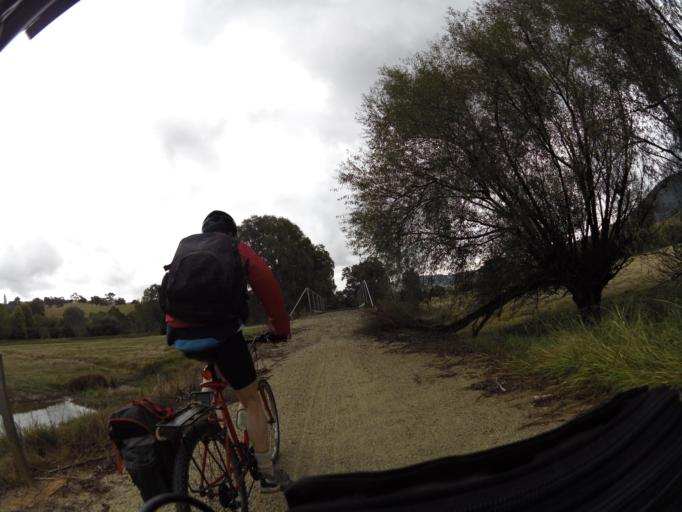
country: AU
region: New South Wales
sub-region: Albury Municipality
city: East Albury
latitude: -36.1936
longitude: 147.3183
